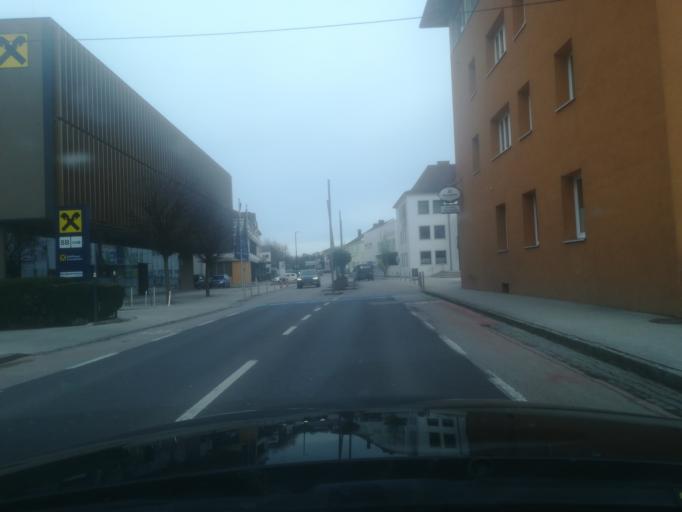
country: AT
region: Upper Austria
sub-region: Wels-Land
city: Thalheim bei Wels
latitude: 48.1531
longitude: 14.0299
